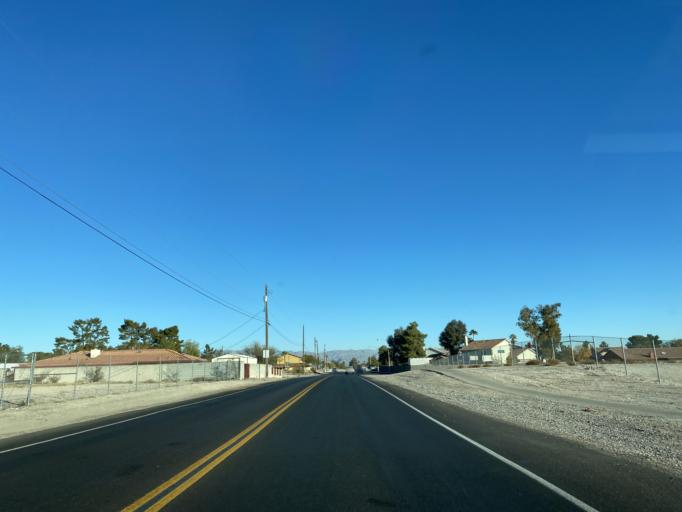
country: US
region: Nevada
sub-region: Clark County
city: Whitney
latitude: 36.0835
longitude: -115.1099
